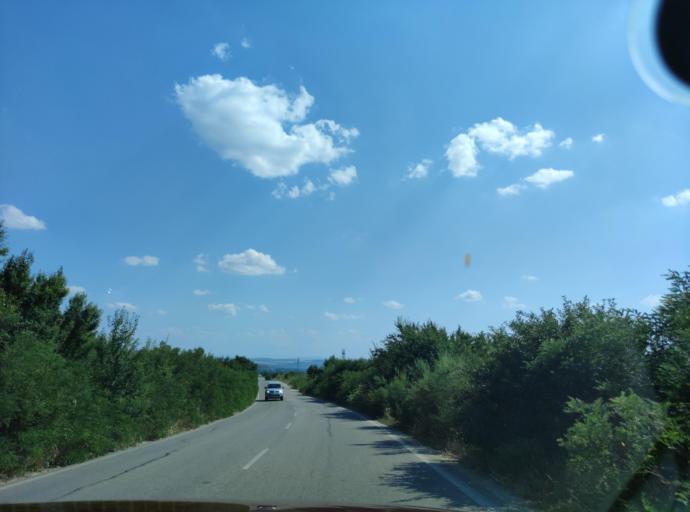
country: BG
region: Pleven
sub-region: Obshtina Cherven Bryag
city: Koynare
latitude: 43.3535
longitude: 24.0641
